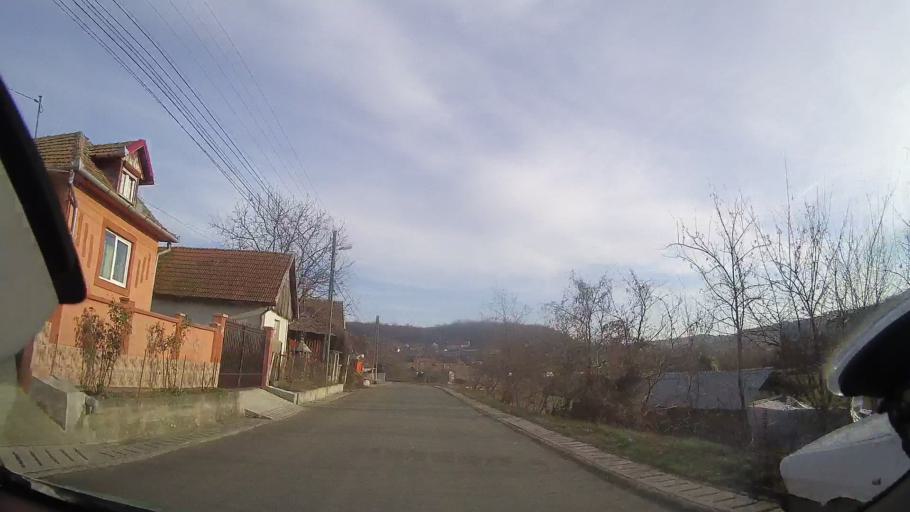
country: RO
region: Bihor
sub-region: Comuna Sarbi
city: Burzuc
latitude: 47.1563
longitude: 22.1659
